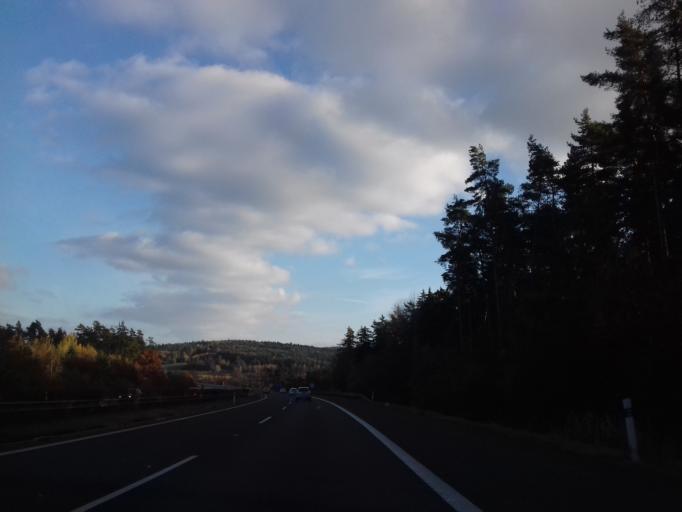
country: CZ
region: Plzensky
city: Dobrany
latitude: 49.6800
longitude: 13.3066
